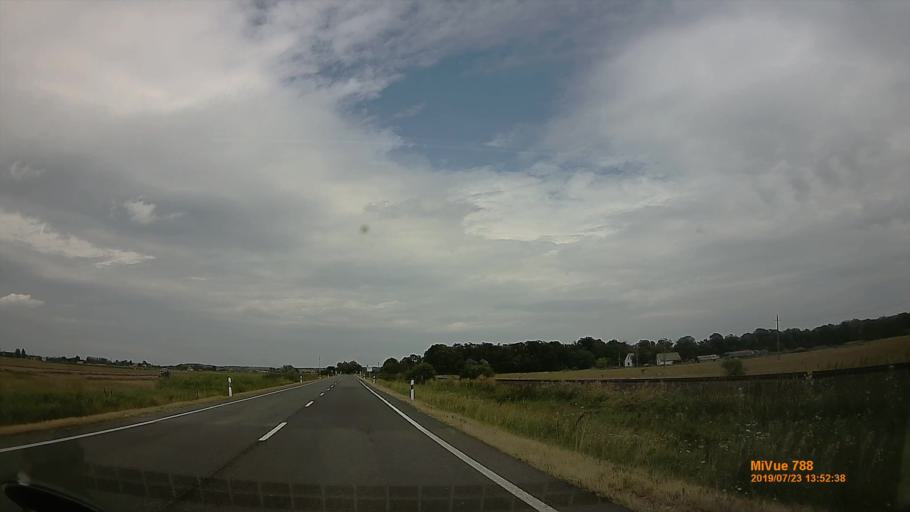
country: HU
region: Hajdu-Bihar
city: Polgar
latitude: 47.9044
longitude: 21.1633
